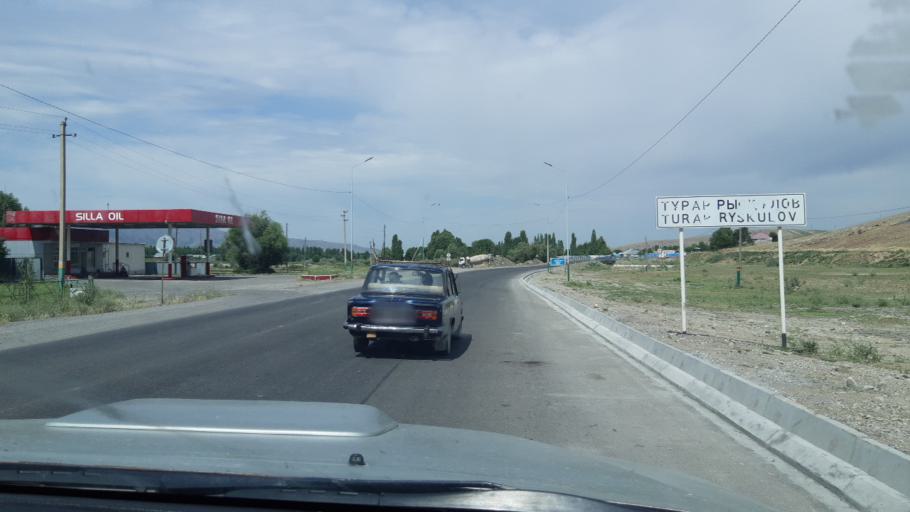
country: KZ
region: Ongtustik Qazaqstan
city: Turar Ryskulov
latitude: 42.5494
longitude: 70.3035
